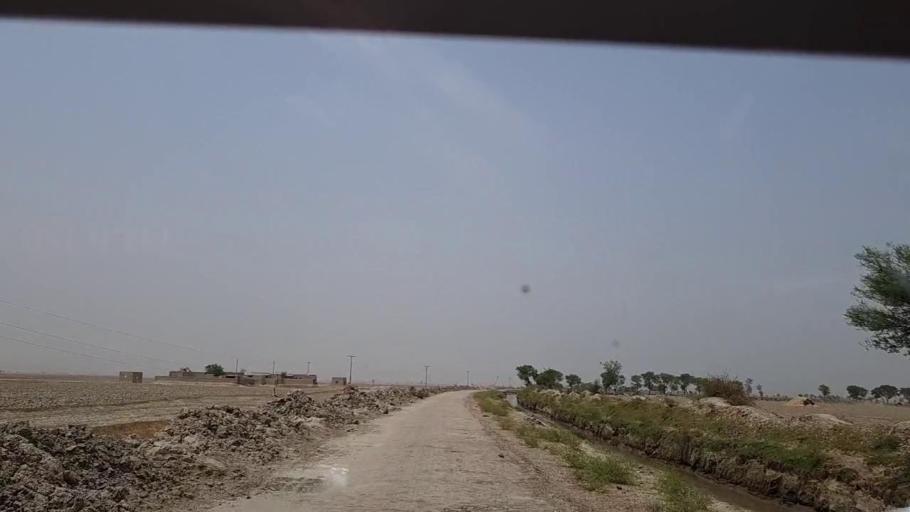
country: PK
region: Sindh
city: Khairpur Nathan Shah
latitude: 27.0385
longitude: 67.6187
